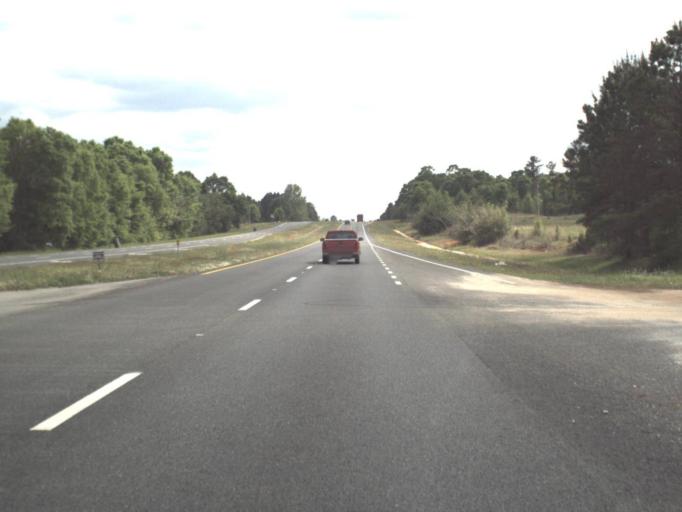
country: US
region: Florida
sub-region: Escambia County
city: Century
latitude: 30.9133
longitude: -87.3154
